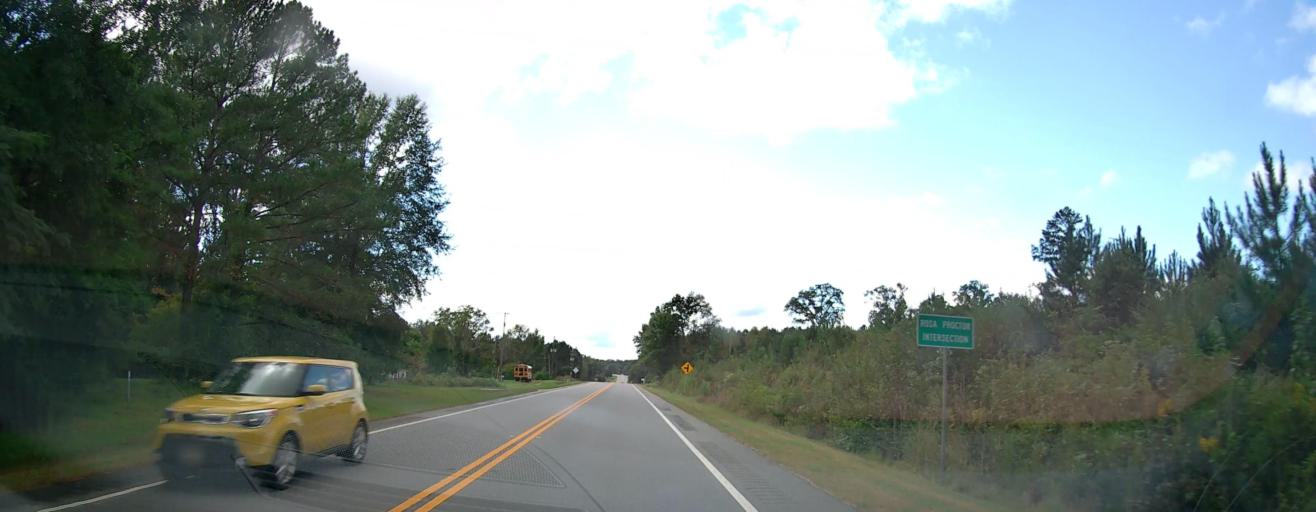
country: US
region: Georgia
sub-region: Baldwin County
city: Milledgeville
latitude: 33.0749
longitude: -83.3341
